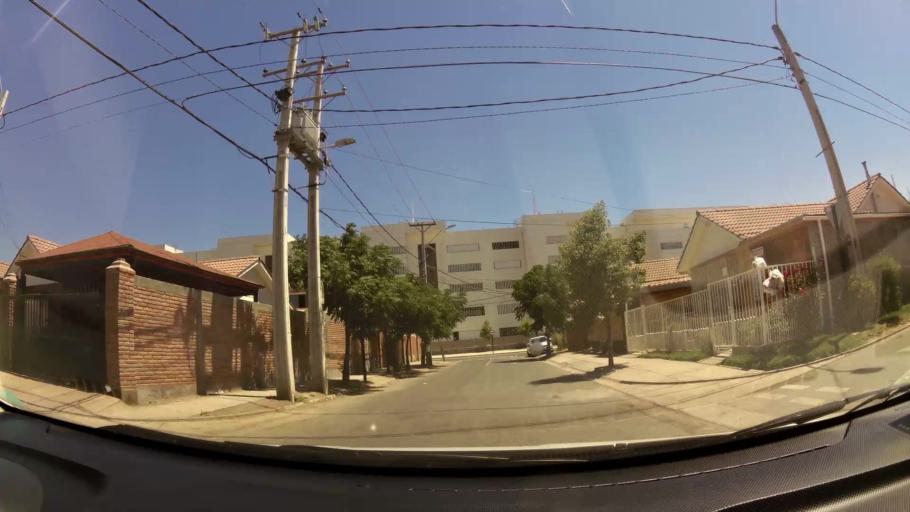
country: CL
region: O'Higgins
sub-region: Provincia de Cachapoal
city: Rancagua
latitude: -34.1559
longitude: -70.7653
